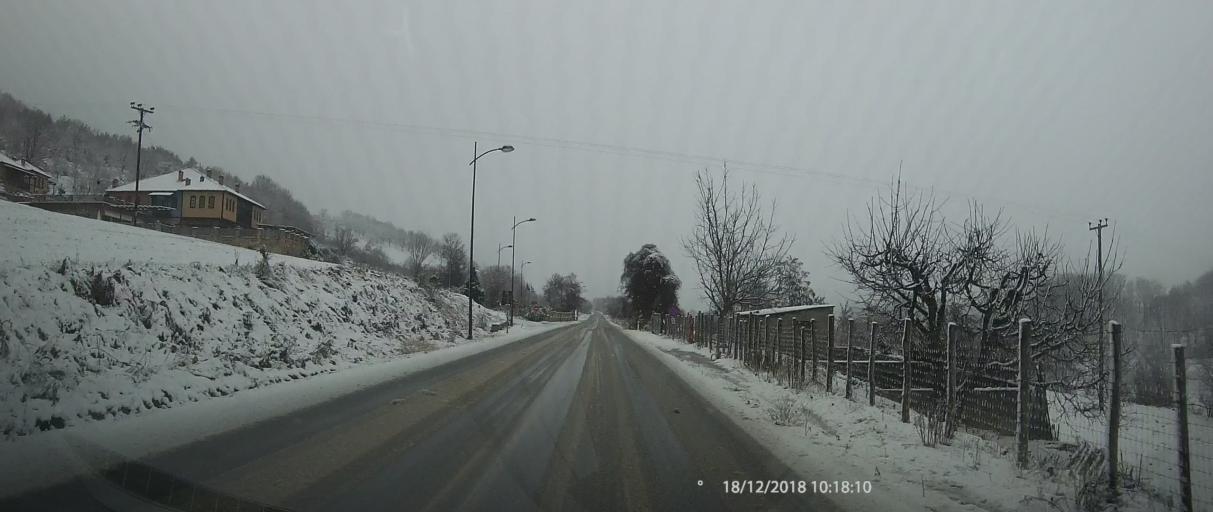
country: GR
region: Thessaly
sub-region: Nomos Larisis
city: Livadi
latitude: 40.1295
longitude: 22.2156
